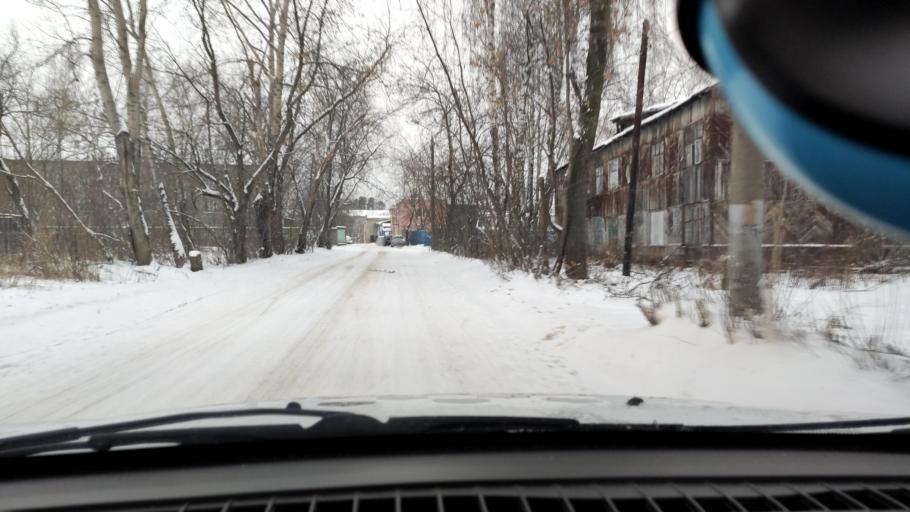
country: RU
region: Perm
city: Kondratovo
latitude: 58.0240
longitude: 56.0183
